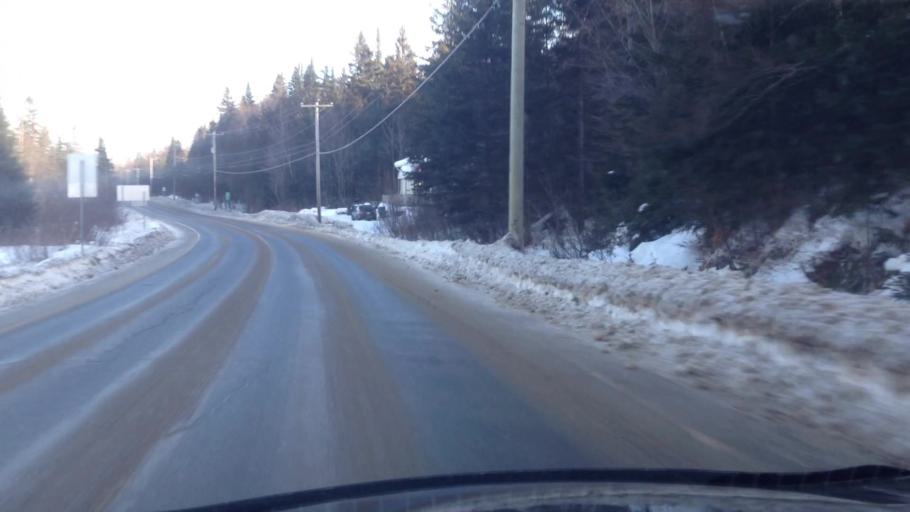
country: CA
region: Quebec
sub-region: Laurentides
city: Sainte-Agathe-des-Monts
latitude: 45.9100
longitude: -74.3433
